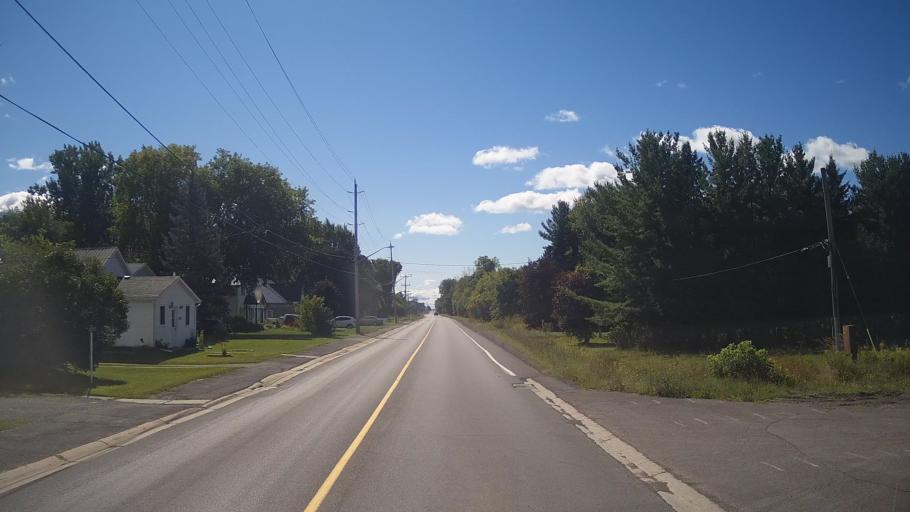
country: US
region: New York
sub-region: St. Lawrence County
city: Norfolk
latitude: 44.9723
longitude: -75.2417
